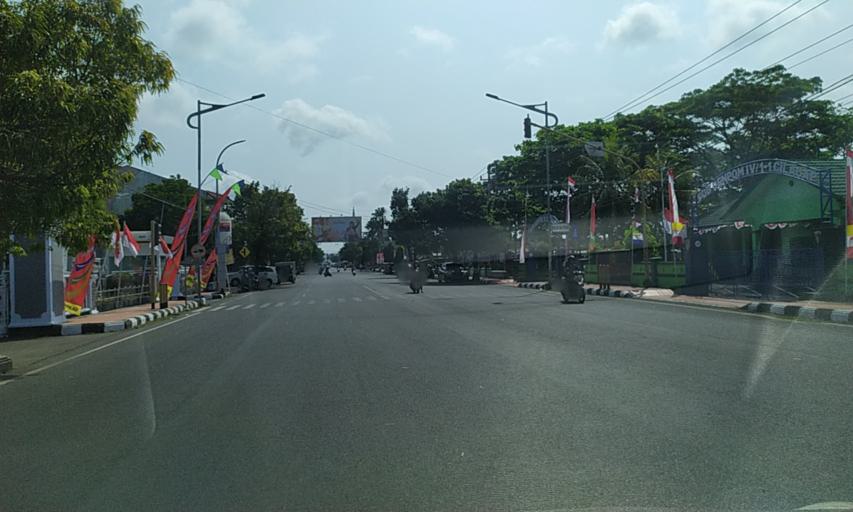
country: ID
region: Central Java
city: Karangbadar Kidul
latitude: -7.7279
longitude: 109.0133
